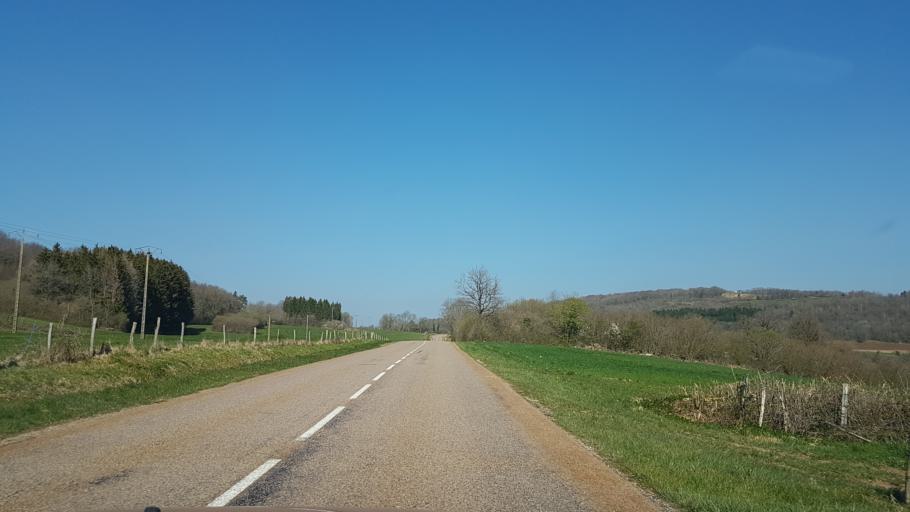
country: FR
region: Franche-Comte
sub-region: Departement du Jura
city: Orgelet
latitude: 46.5370
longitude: 5.6469
